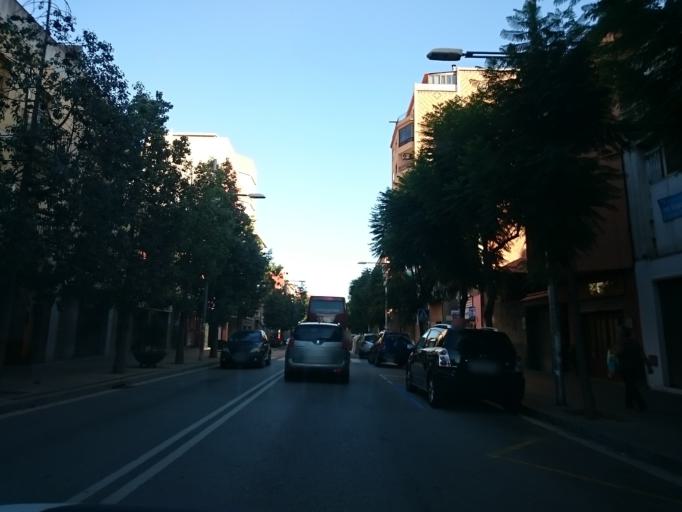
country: ES
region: Catalonia
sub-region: Provincia de Barcelona
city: Sant Andreu de la Barca
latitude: 41.4477
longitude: 1.9750
